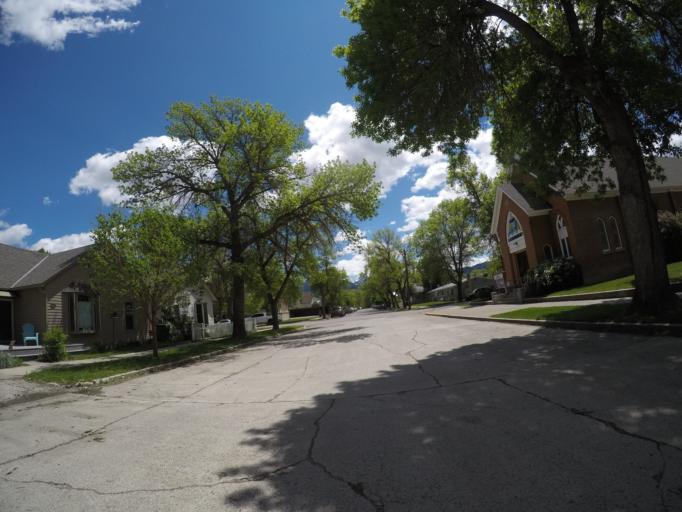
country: US
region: Montana
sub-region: Park County
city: Livingston
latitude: 45.6584
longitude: -110.5603
